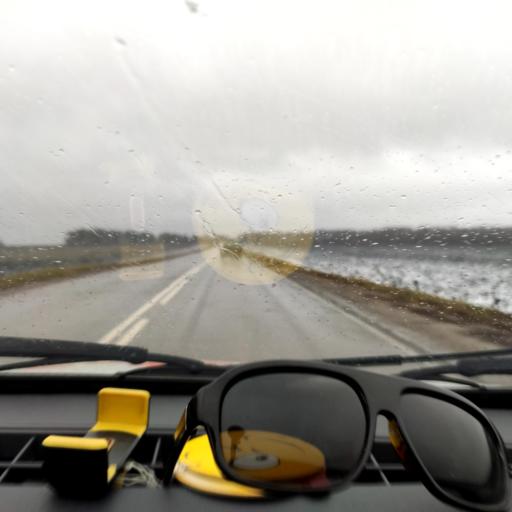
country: RU
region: Bashkortostan
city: Iglino
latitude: 54.8773
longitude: 56.5329
